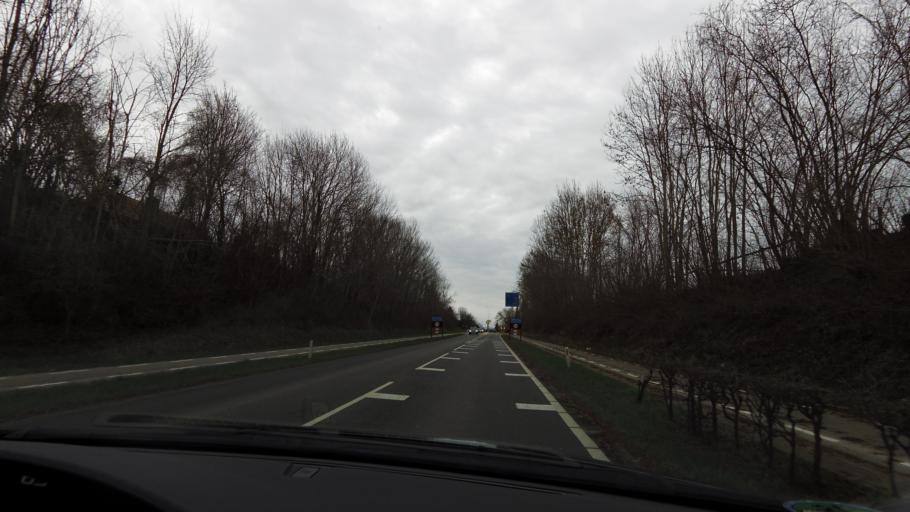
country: NL
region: Limburg
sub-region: Gemeente Maastricht
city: Heer
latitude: 50.8330
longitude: 5.7561
